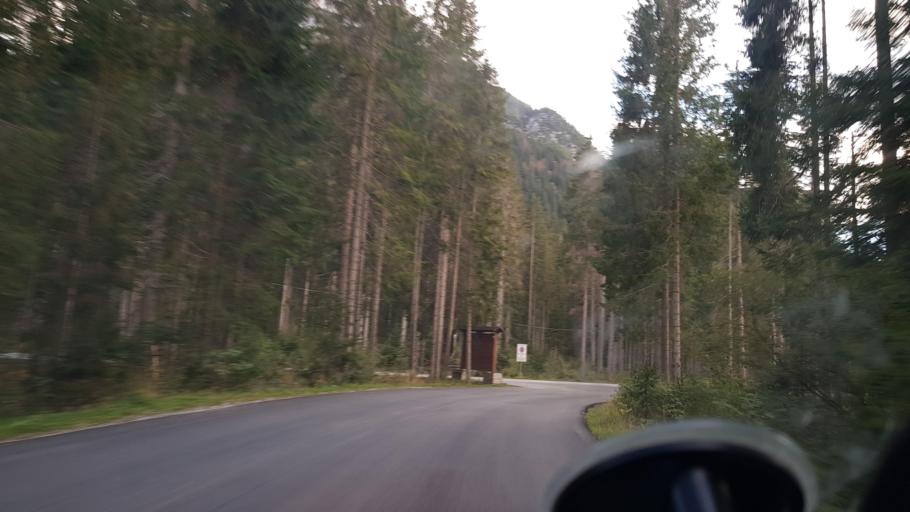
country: IT
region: Veneto
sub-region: Provincia di Belluno
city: San Pietro di Cadore
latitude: 46.6147
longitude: 12.6330
